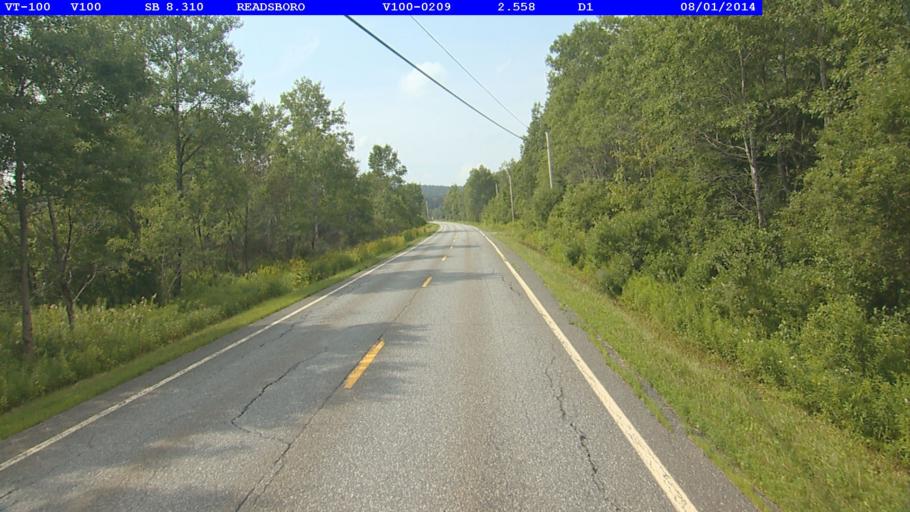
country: US
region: Massachusetts
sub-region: Berkshire County
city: North Adams
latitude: 42.8246
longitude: -72.9835
